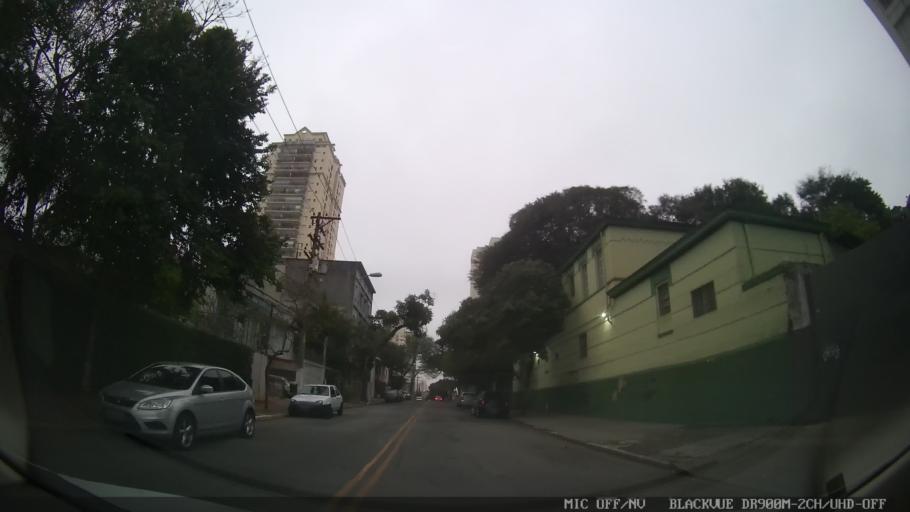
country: BR
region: Sao Paulo
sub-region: Sao Paulo
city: Sao Paulo
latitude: -23.5925
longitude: -46.6078
